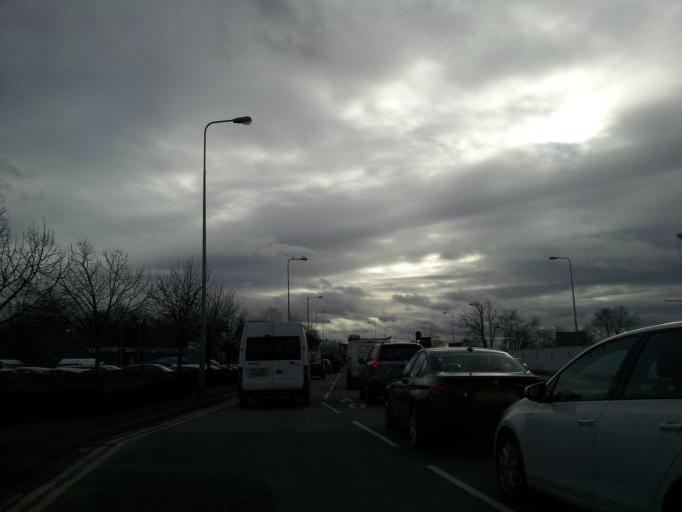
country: GB
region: England
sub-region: Staffordshire
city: Stafford
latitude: 52.8056
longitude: -2.1110
